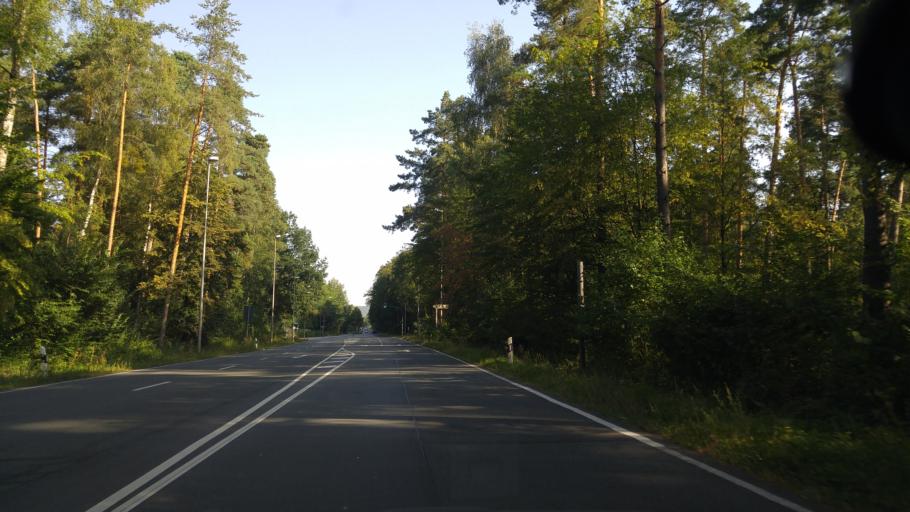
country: DE
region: Bavaria
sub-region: Regierungsbezirk Mittelfranken
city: Buckenhof
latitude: 49.5803
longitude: 11.0333
